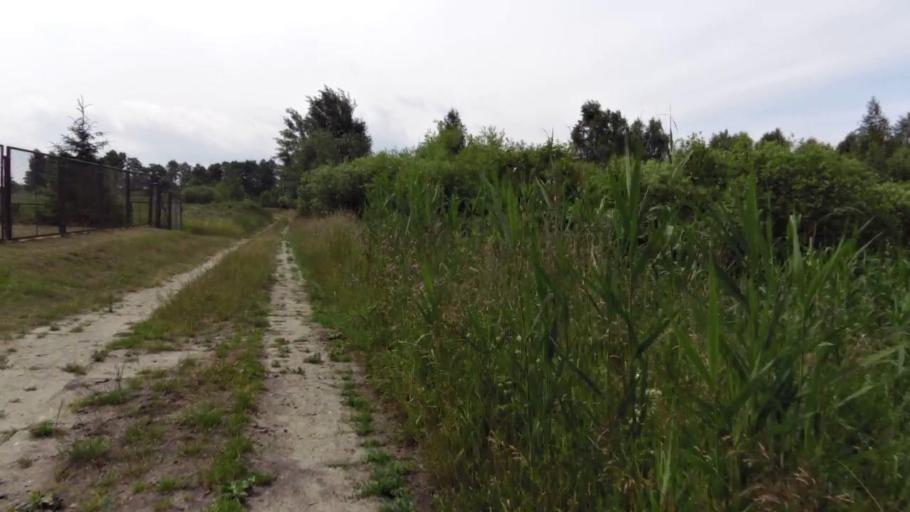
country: PL
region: West Pomeranian Voivodeship
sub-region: Powiat goleniowski
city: Stepnica
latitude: 53.7305
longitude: 14.6028
